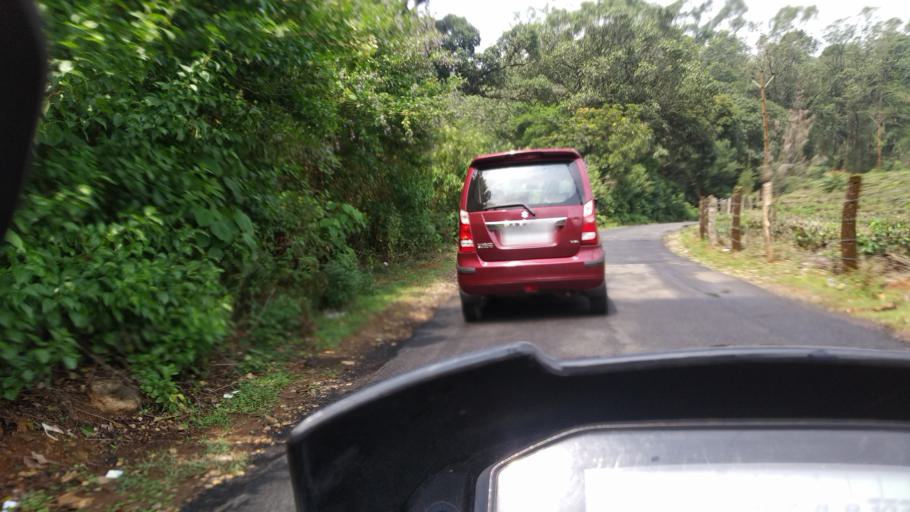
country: IN
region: Kerala
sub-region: Kottayam
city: Erattupetta
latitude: 9.6321
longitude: 76.9621
